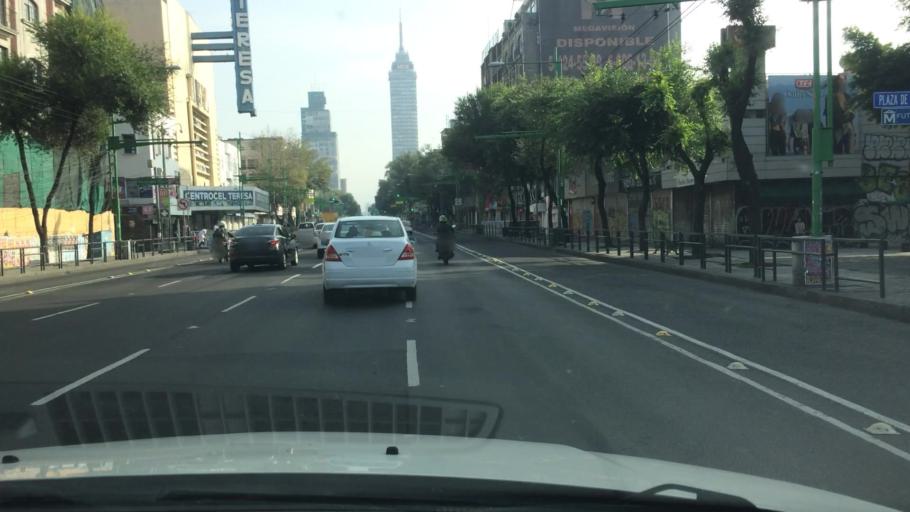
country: MX
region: Mexico City
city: Mexico City
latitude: 19.4274
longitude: -99.1419
